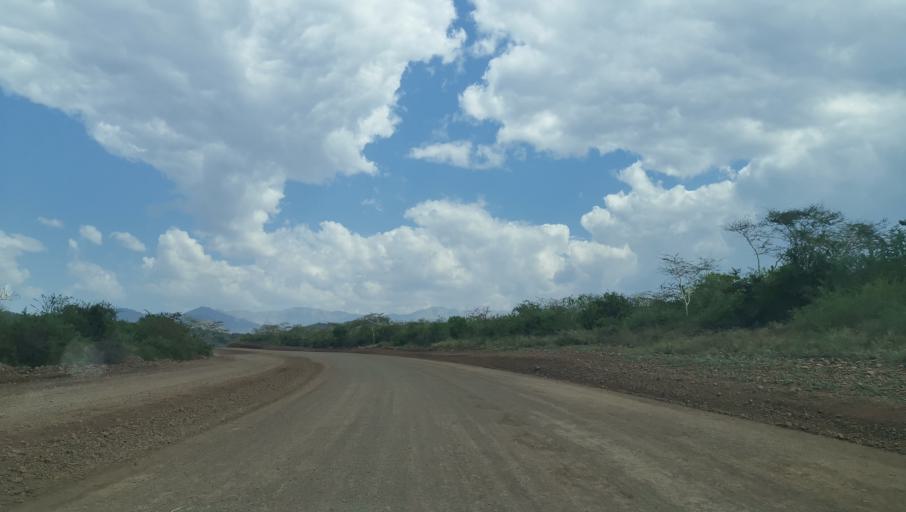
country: ET
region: Southern Nations, Nationalities, and People's Region
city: Felege Neway
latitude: 6.3619
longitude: 37.2896
